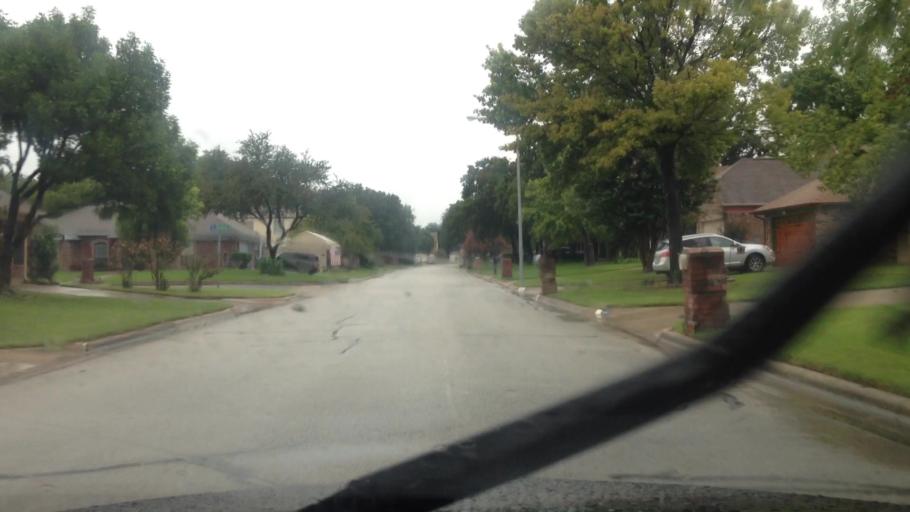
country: US
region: Texas
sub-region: Tarrant County
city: Watauga
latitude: 32.8842
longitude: -97.2311
